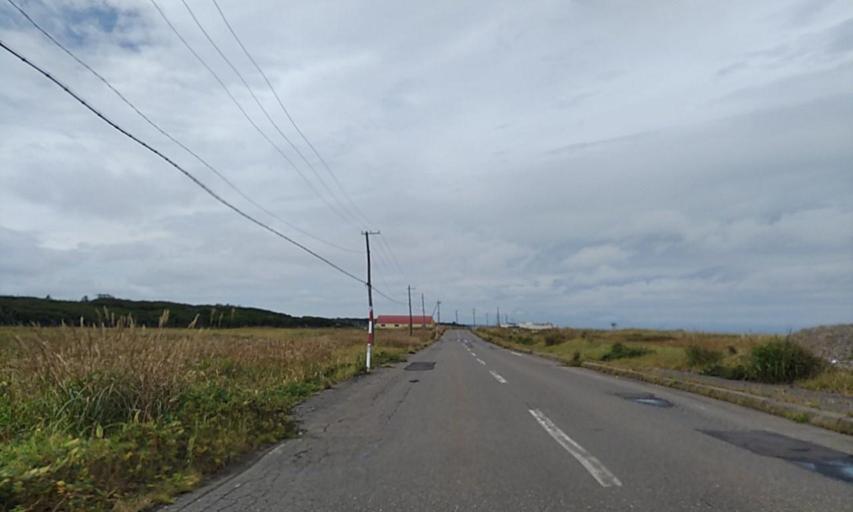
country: JP
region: Hokkaido
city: Shibetsu
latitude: 43.6076
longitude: 145.2822
